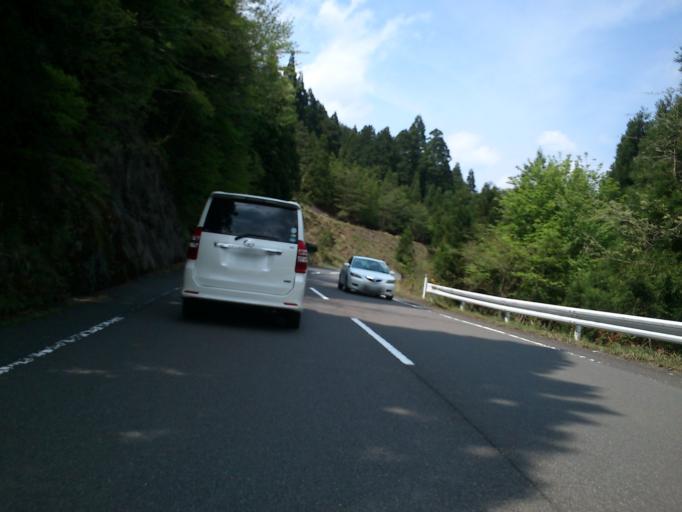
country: JP
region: Hyogo
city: Toyooka
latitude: 35.4055
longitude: 134.9498
